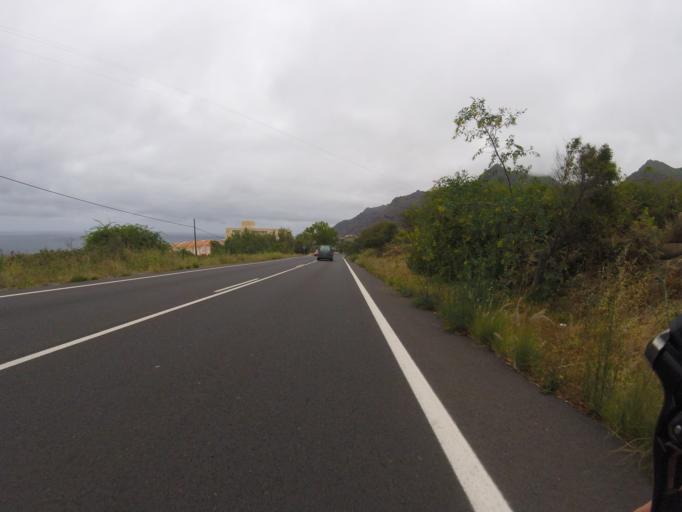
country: ES
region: Canary Islands
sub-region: Provincia de Santa Cruz de Tenerife
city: Tegueste
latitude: 28.5437
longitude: -16.3546
